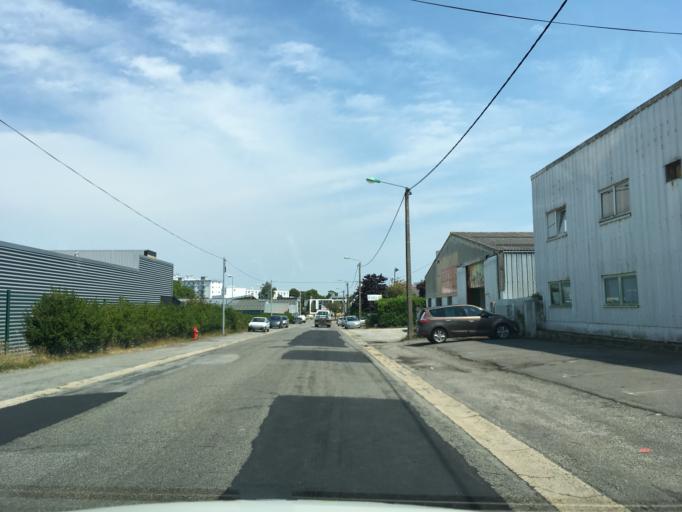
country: FR
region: Brittany
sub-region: Departement du Morbihan
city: Queven
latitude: 47.7618
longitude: -3.3990
